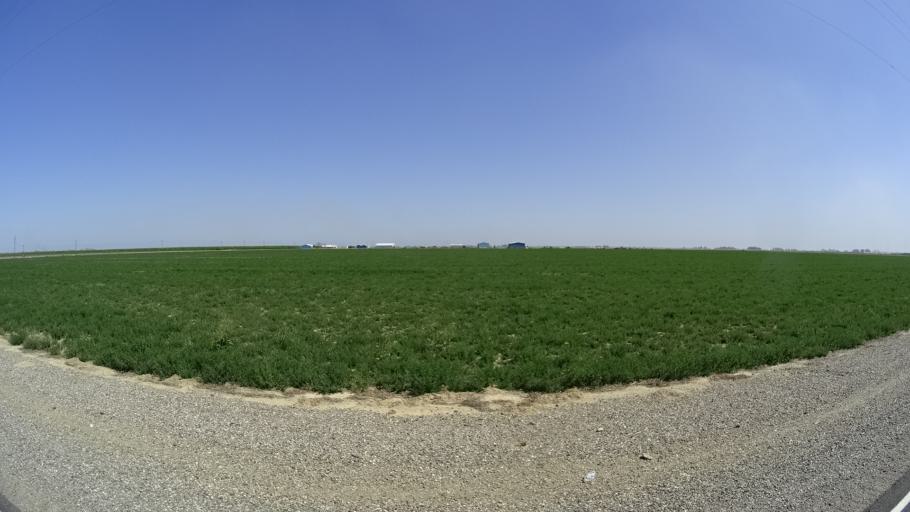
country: US
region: California
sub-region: Glenn County
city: Willows
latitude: 39.6015
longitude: -122.1375
